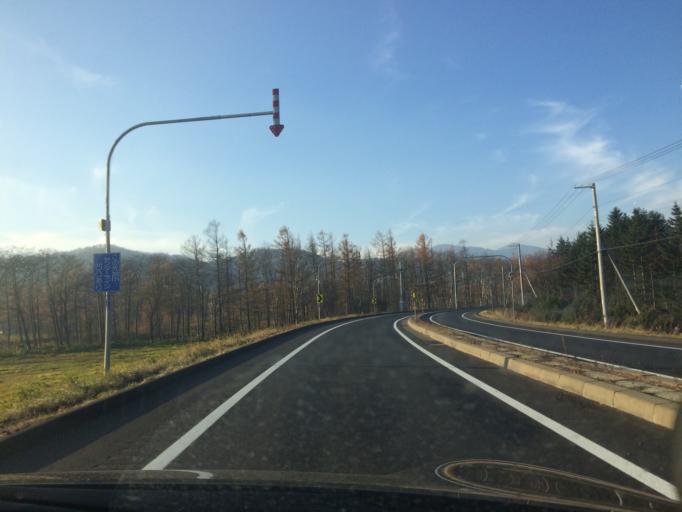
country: JP
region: Hokkaido
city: Otofuke
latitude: 42.9839
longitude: 142.8378
